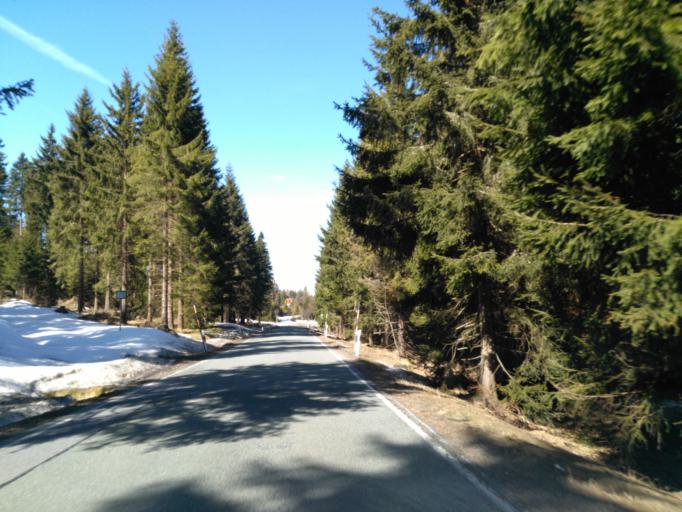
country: DE
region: Saxony
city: Kurort Oberwiesenthal
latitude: 50.4328
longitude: 12.8998
